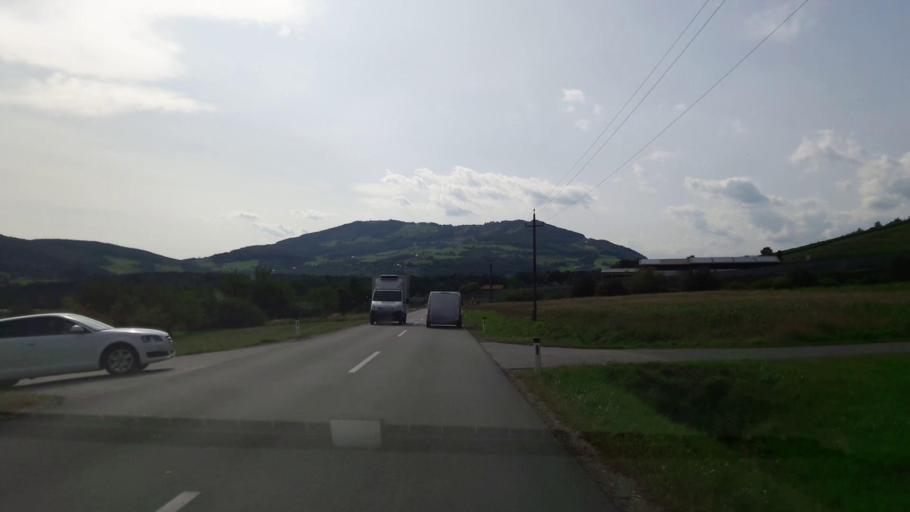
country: AT
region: Styria
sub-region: Politischer Bezirk Hartberg-Fuerstenfeld
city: Stubenberg
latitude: 47.2351
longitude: 15.8300
